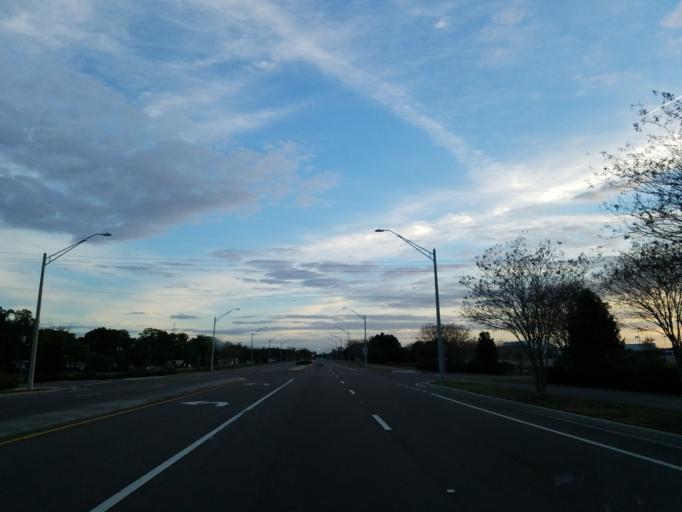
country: US
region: Florida
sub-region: Hillsborough County
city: Egypt Lake-Leto
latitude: 27.9872
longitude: -82.5201
